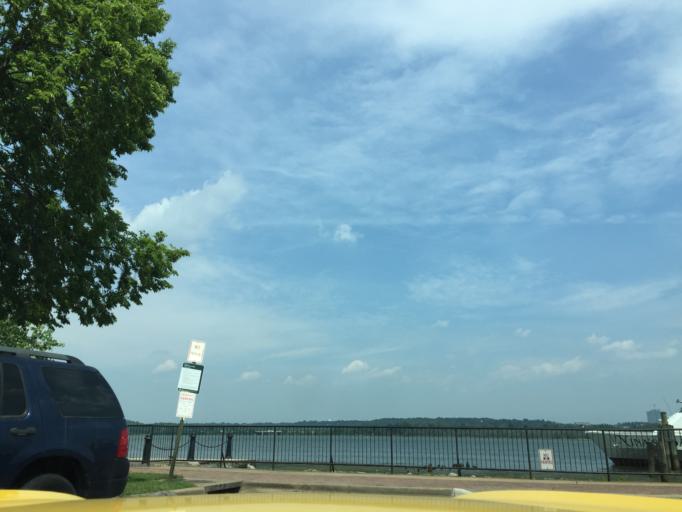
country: US
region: Virginia
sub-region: City of Alexandria
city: Alexandria
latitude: 38.8030
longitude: -77.0393
